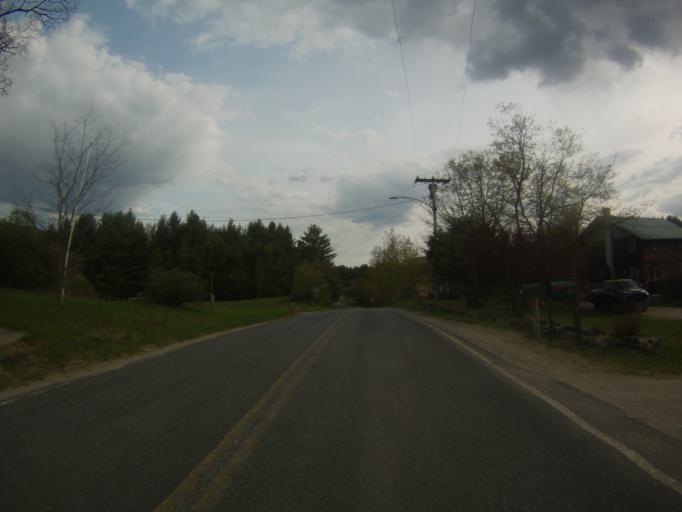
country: US
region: New York
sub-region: Warren County
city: Warrensburg
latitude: 43.8016
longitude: -73.9400
